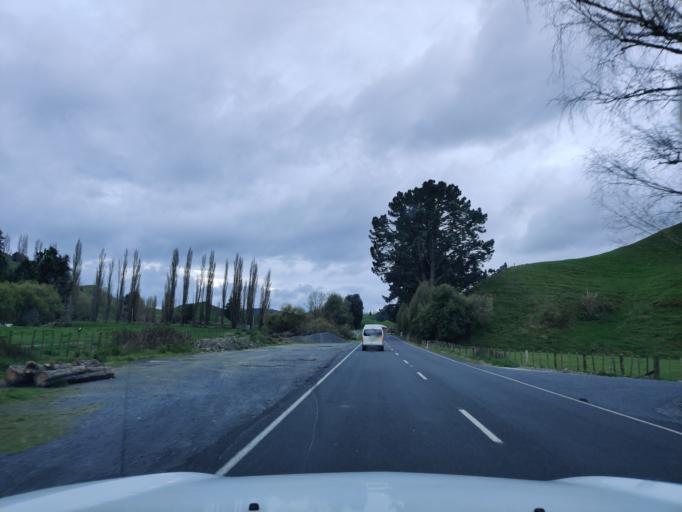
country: NZ
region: Waikato
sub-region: Otorohanga District
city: Otorohanga
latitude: -38.4754
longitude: 175.1742
